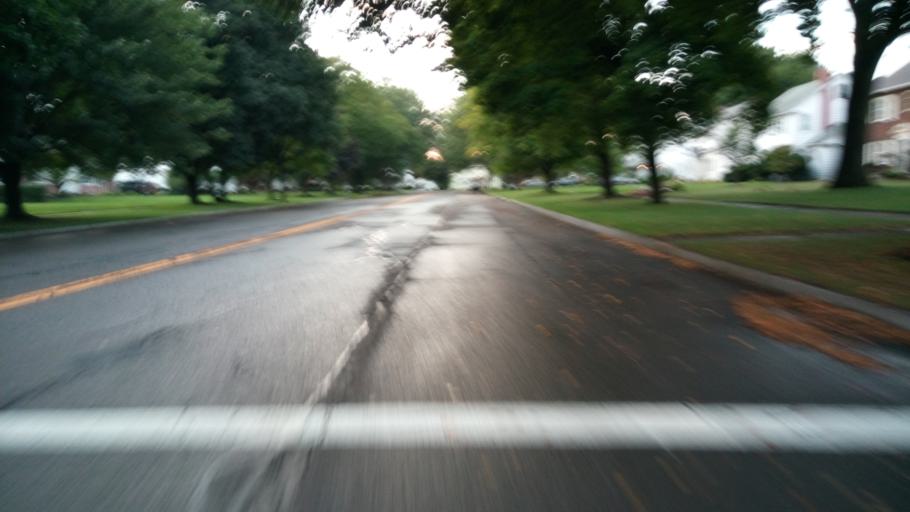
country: US
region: New York
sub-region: Chemung County
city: Elmira
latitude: 42.0940
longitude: -76.8253
